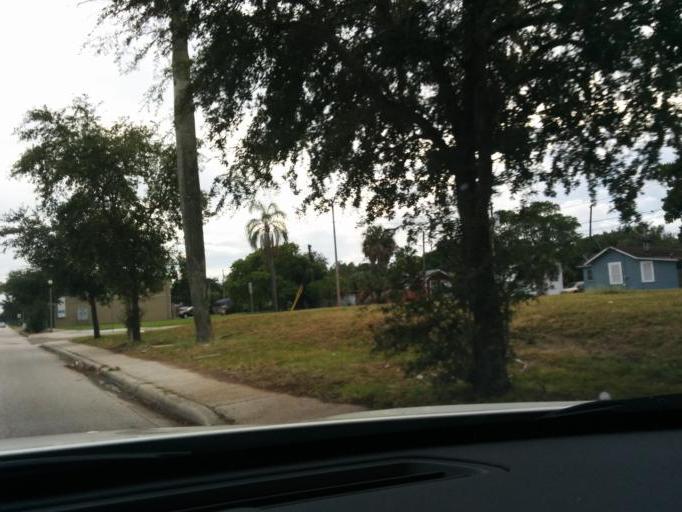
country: US
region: Florida
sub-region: Pinellas County
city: Saint Petersburg
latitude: 27.7576
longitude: -82.6385
